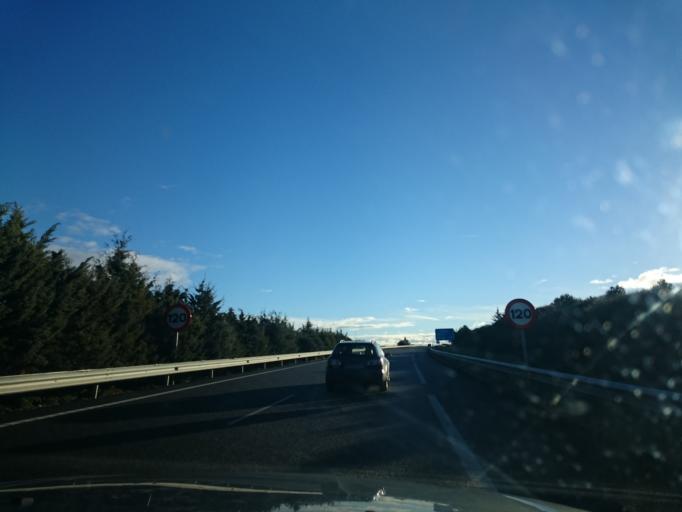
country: ES
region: Castille and Leon
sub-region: Provincia de Leon
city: Bercianos del Real Camino
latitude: 42.3926
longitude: -5.1343
